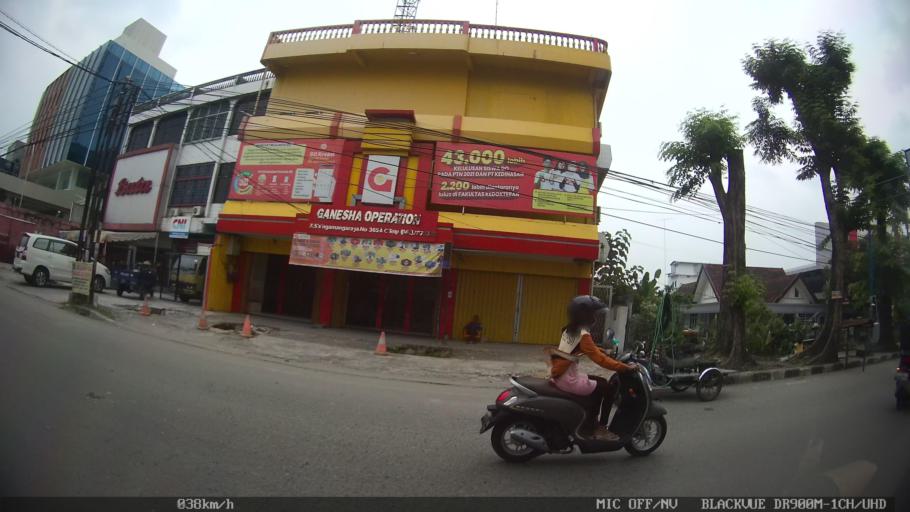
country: ID
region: North Sumatra
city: Medan
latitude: 3.5533
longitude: 98.6959
